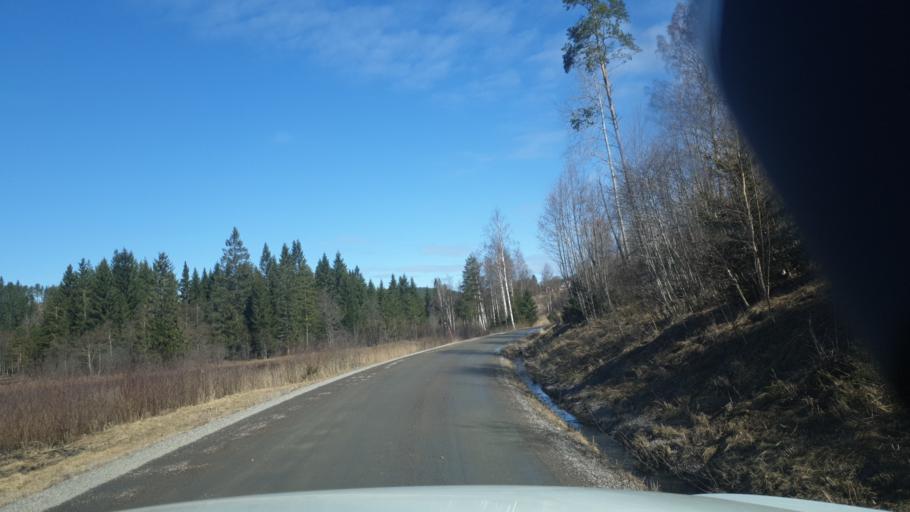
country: NO
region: Ostfold
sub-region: Romskog
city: Romskog
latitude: 59.6745
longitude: 11.9328
